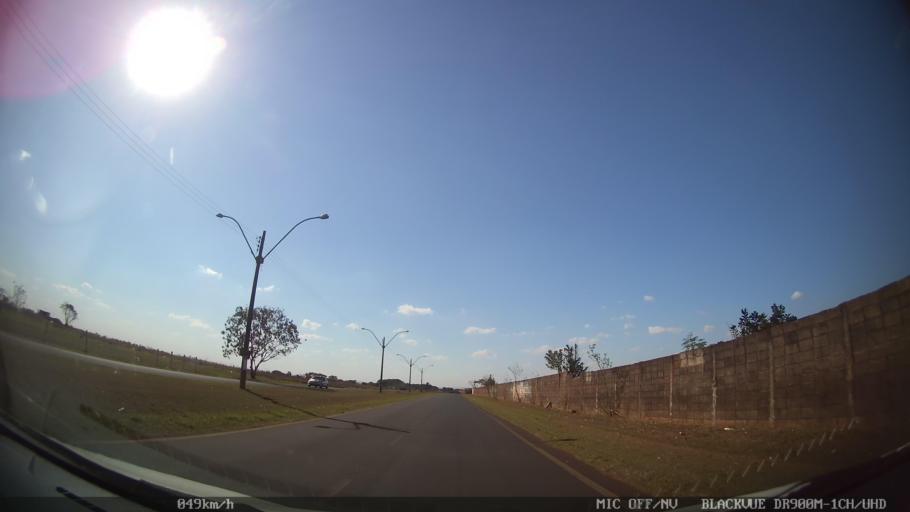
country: BR
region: Sao Paulo
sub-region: Ribeirao Preto
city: Ribeirao Preto
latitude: -21.1475
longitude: -47.7706
